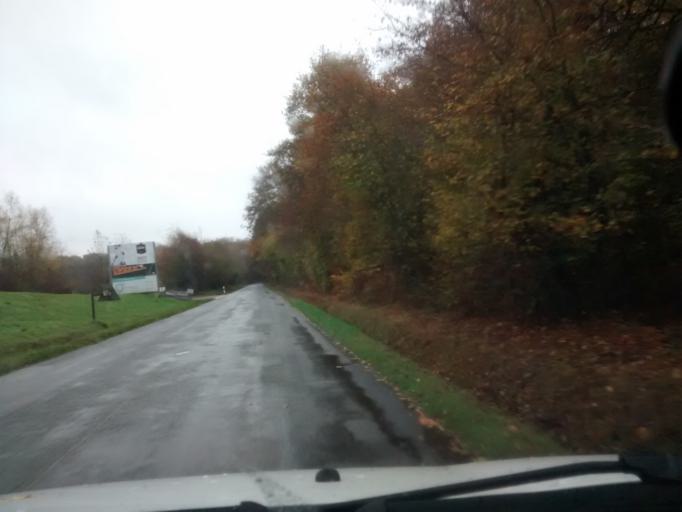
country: FR
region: Brittany
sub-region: Departement d'Ille-et-Vilaine
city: Vern-sur-Seiche
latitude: 48.0675
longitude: -1.6033
